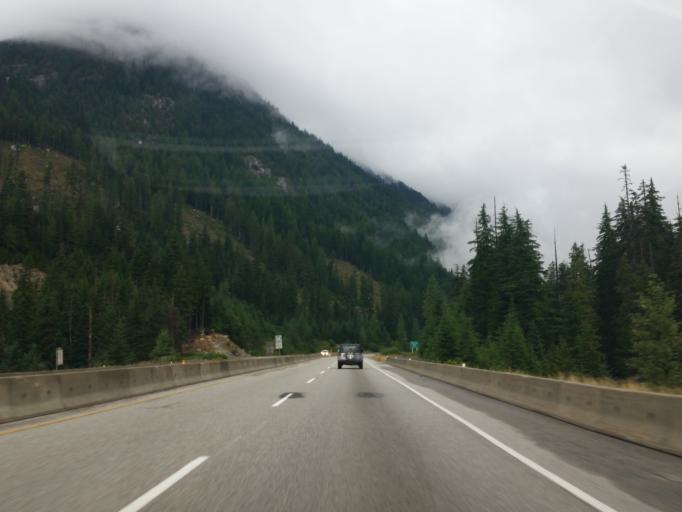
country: CA
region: British Columbia
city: Hope
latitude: 49.5694
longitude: -121.1827
